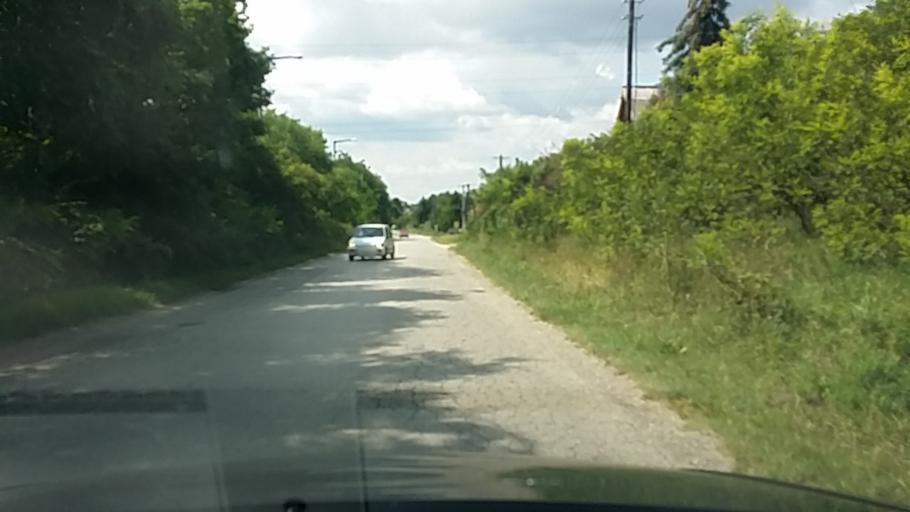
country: HU
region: Bacs-Kiskun
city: Kecskemet
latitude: 46.9193
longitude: 19.6544
